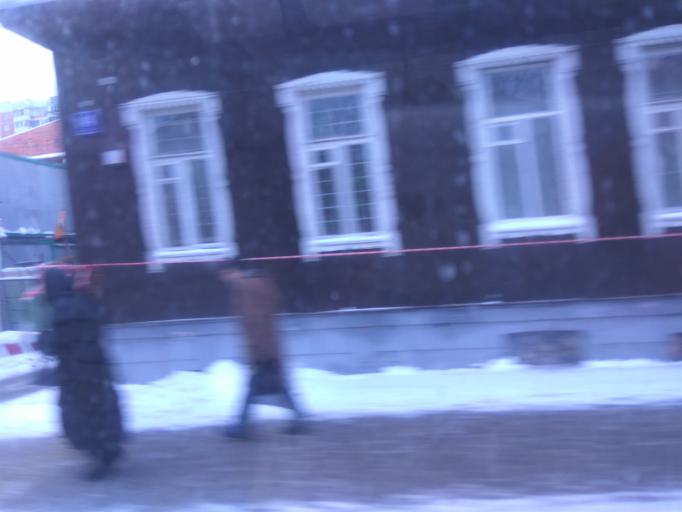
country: RU
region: Moscow
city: Sokol'niki
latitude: 55.7835
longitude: 37.6620
